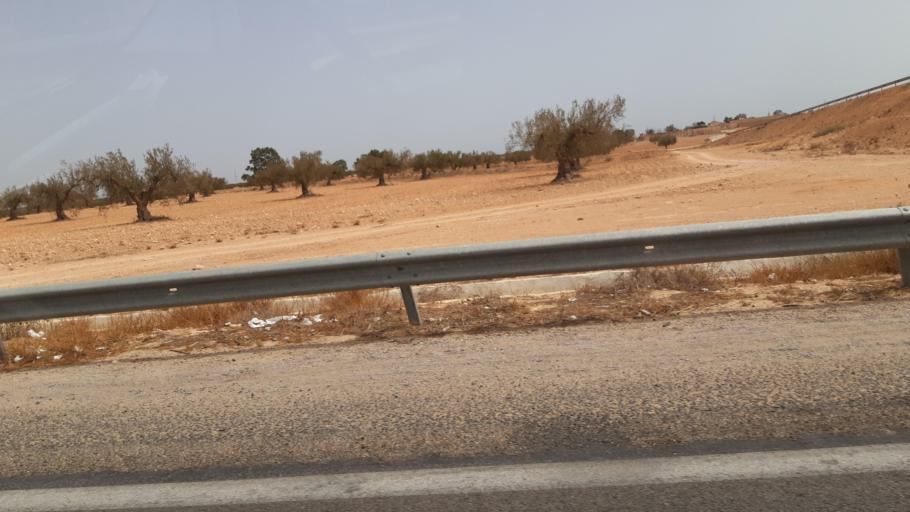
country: TN
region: Safaqis
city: Bi'r `Ali Bin Khalifah
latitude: 34.5880
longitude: 10.4128
